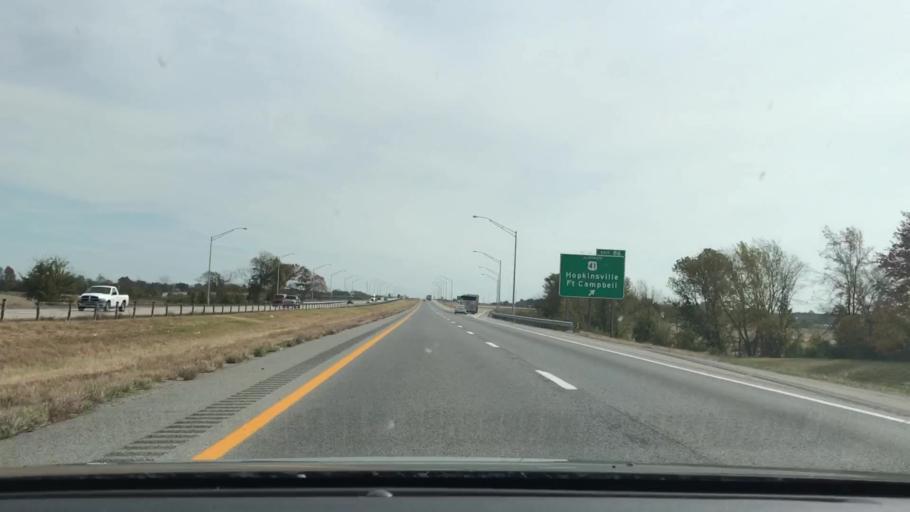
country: US
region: Kentucky
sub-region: Christian County
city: Oak Grove
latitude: 36.7056
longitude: -87.4625
